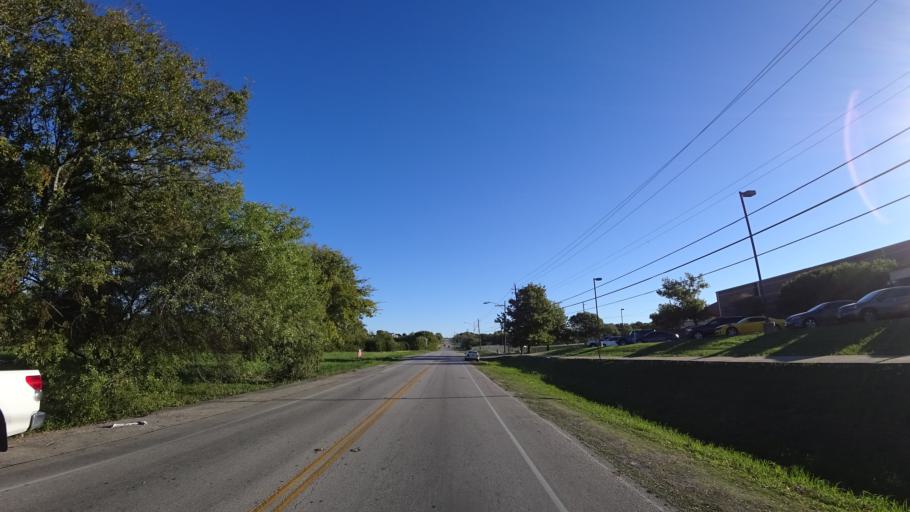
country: US
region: Texas
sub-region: Travis County
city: Hornsby Bend
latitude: 30.3012
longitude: -97.6476
